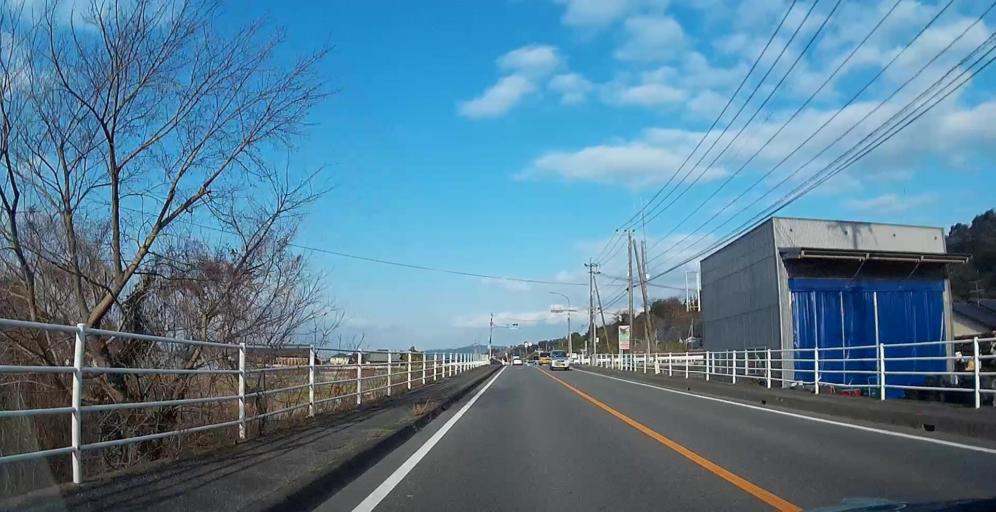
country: JP
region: Kumamoto
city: Matsubase
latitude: 32.5645
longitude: 130.6873
